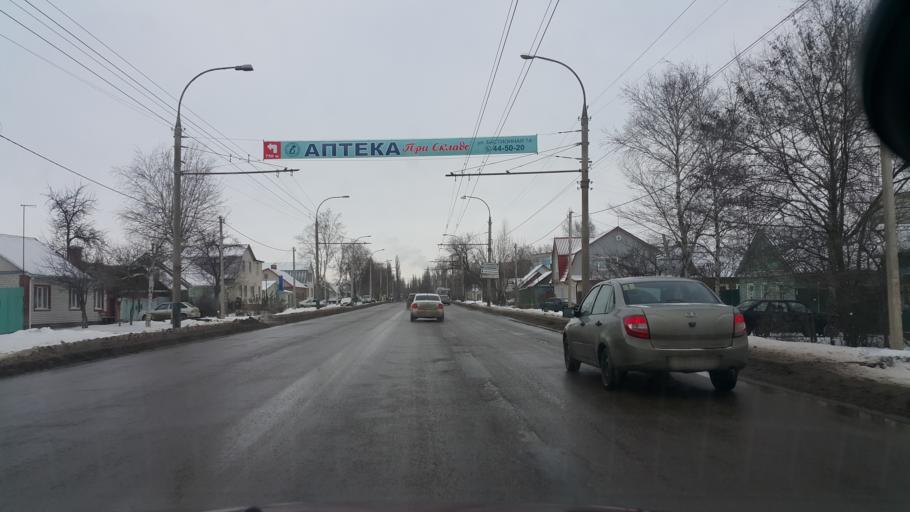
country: RU
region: Tambov
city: Tambov
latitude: 52.7302
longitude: 41.4024
